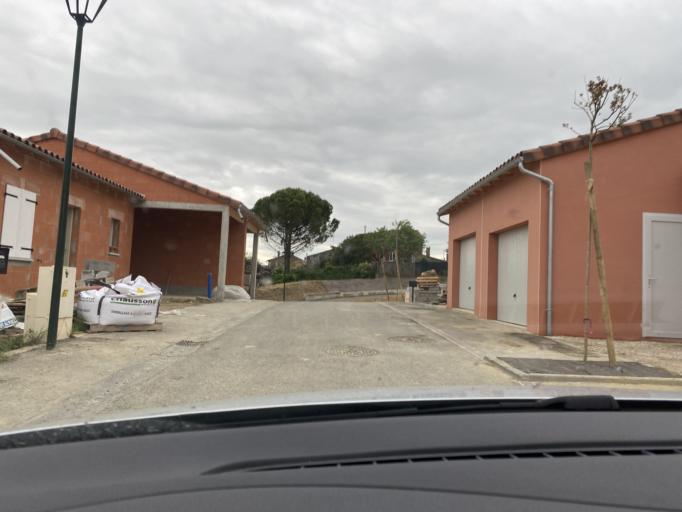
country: FR
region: Midi-Pyrenees
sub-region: Departement de la Haute-Garonne
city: Montgiscard
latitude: 43.4734
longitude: 1.5479
